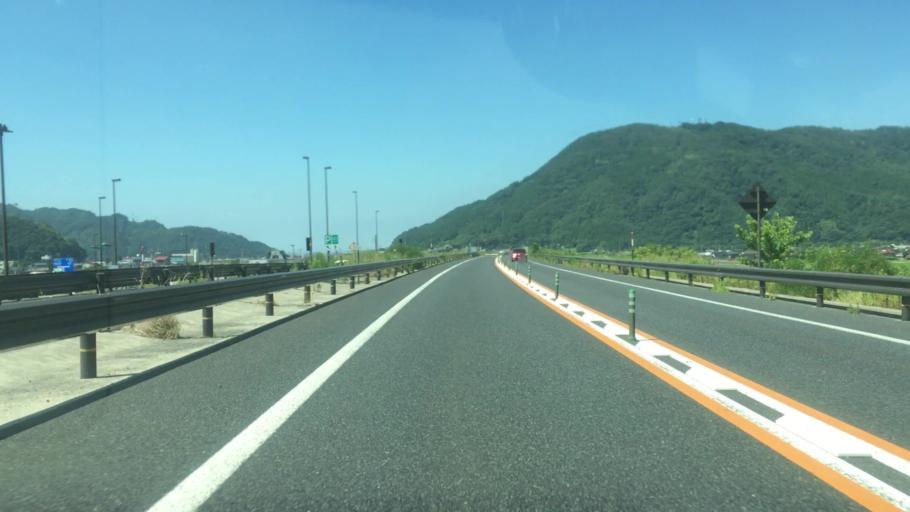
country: JP
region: Tottori
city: Tottori
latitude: 35.3928
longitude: 134.2035
